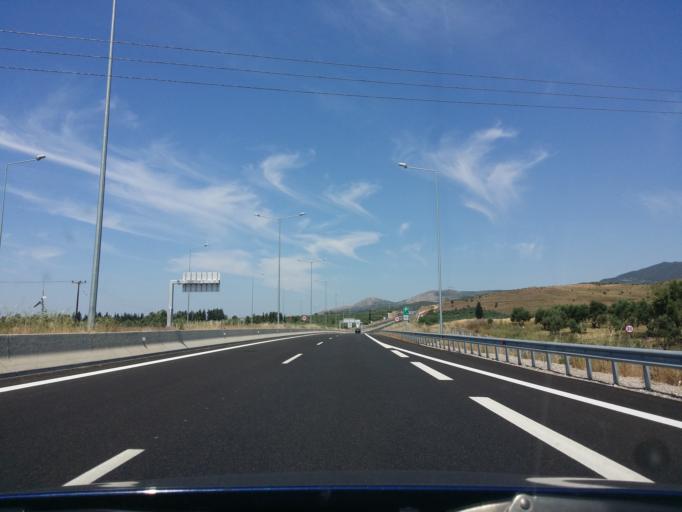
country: GR
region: West Greece
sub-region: Nomos Aitolias kai Akarnanias
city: Mesolongi
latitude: 38.3813
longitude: 21.4952
